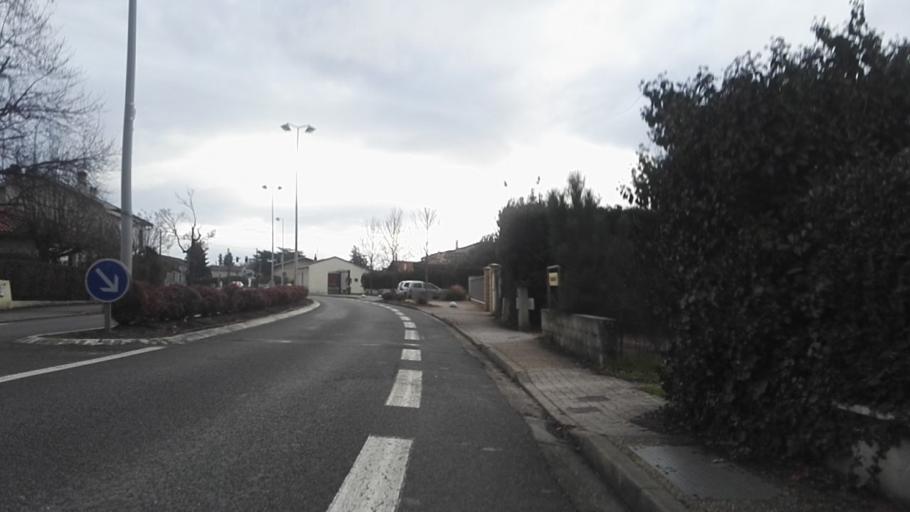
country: FR
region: Aquitaine
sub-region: Departement de la Gironde
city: Eysines
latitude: 44.8663
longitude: -0.6381
